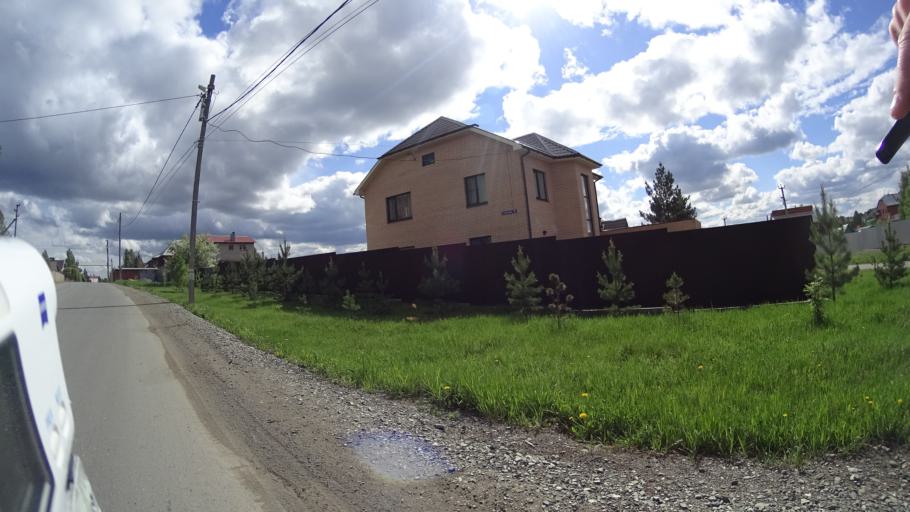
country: RU
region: Chelyabinsk
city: Sargazy
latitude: 55.1612
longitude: 61.2431
